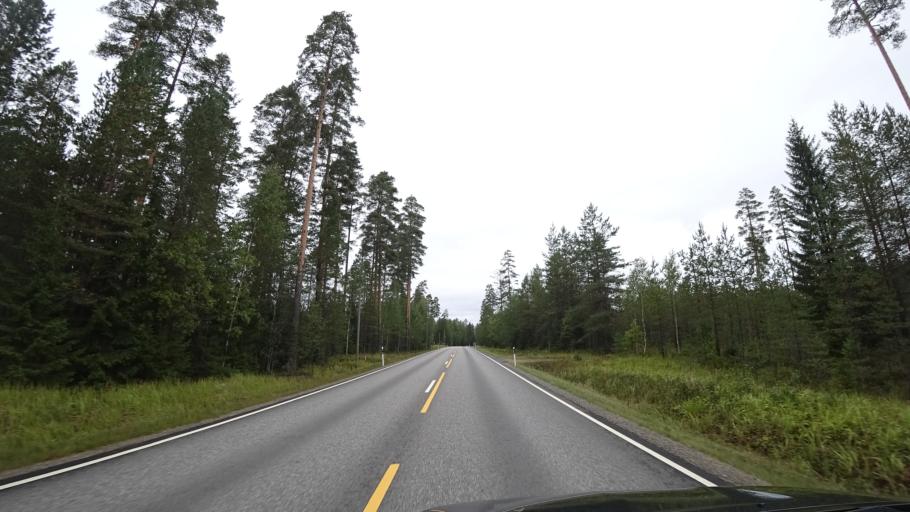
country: FI
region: Paijanne Tavastia
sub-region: Lahti
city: Auttoinen
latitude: 61.2097
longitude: 25.0878
